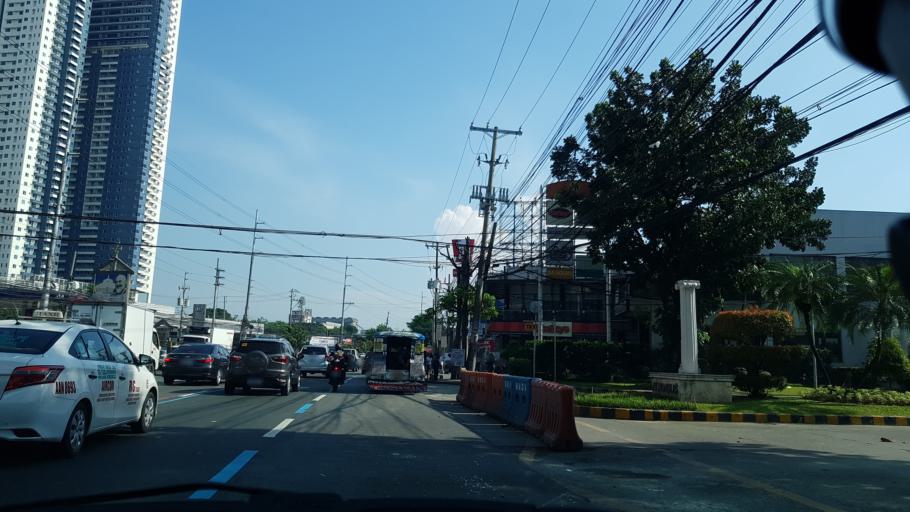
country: PH
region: Metro Manila
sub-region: Marikina
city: Calumpang
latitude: 14.6070
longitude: 121.0787
